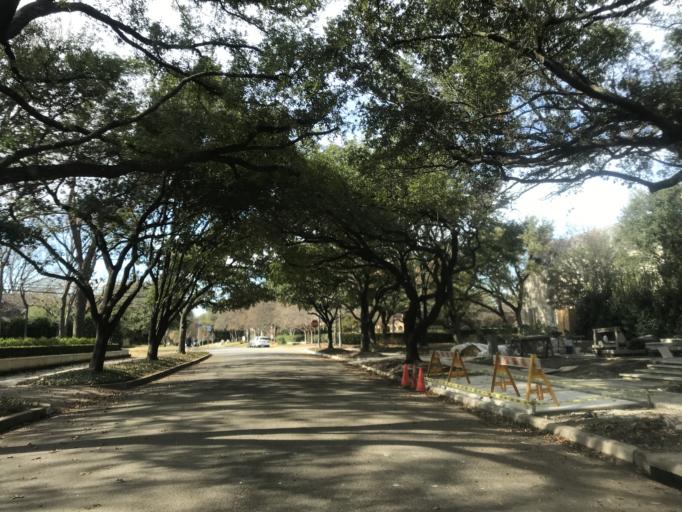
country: US
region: Texas
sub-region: Dallas County
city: Highland Park
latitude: 32.8267
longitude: -96.8062
